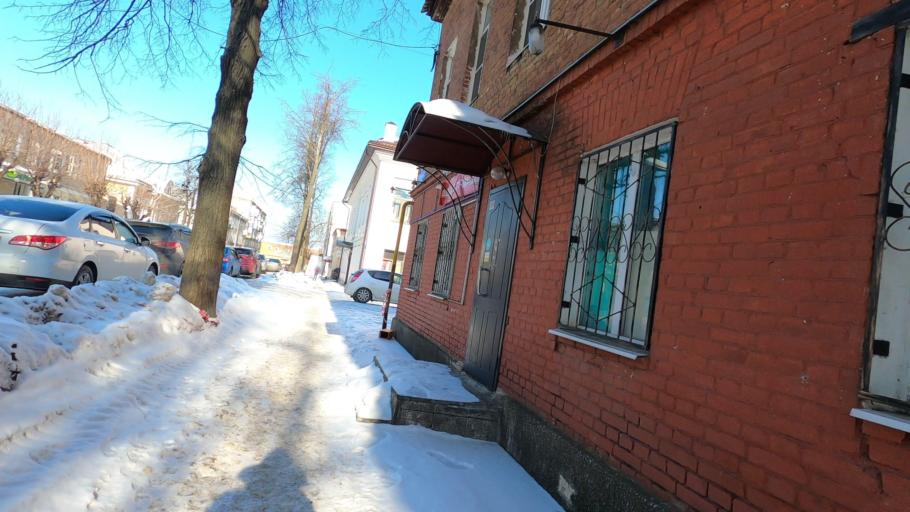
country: RU
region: Jaroslavl
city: Rybinsk
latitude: 58.0491
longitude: 38.8476
